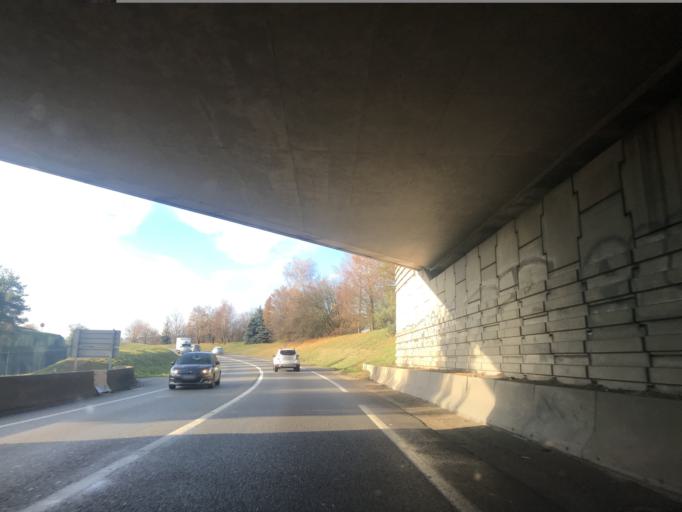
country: FR
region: Rhone-Alpes
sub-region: Departement de la Haute-Savoie
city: Metz-Tessy
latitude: 45.9363
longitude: 6.1037
